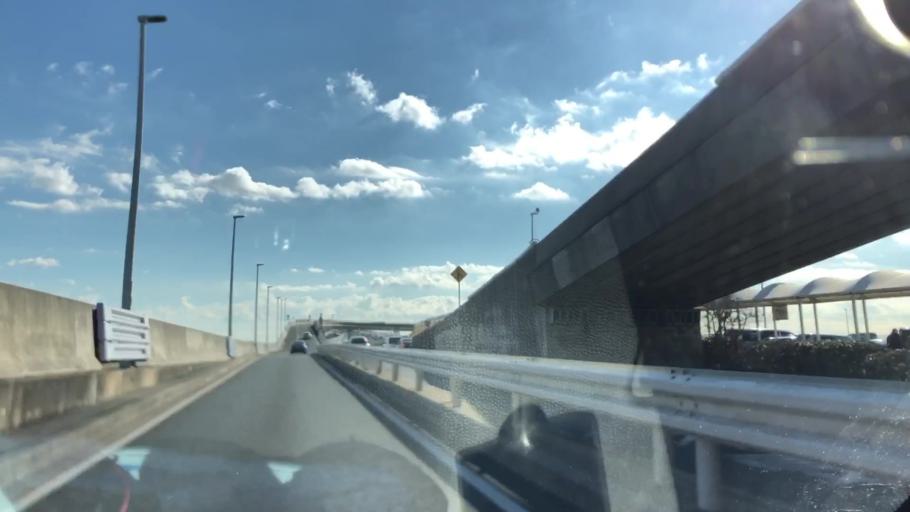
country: JP
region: Chiba
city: Kisarazu
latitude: 35.4641
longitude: 139.8756
